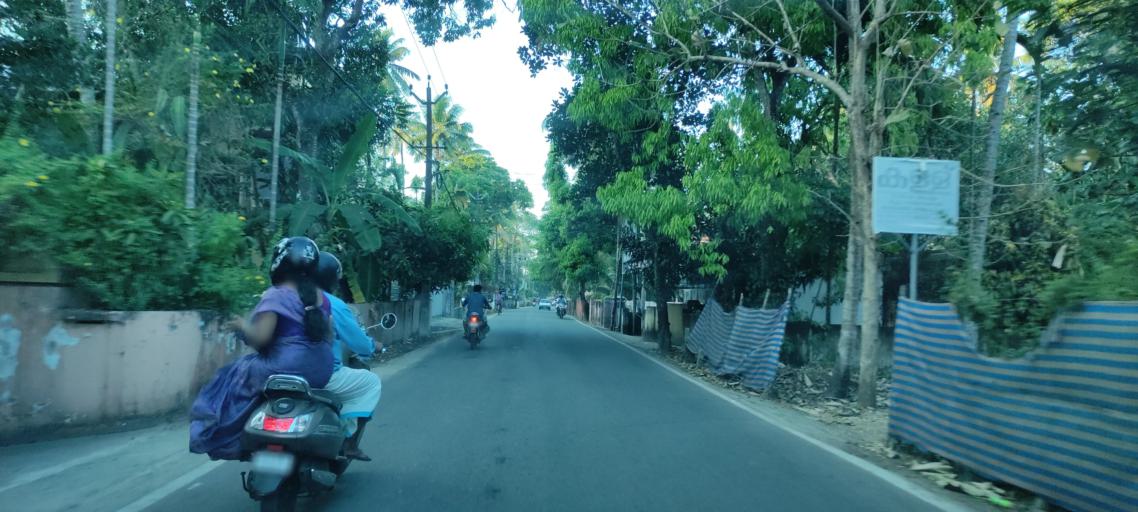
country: IN
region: Kerala
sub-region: Alappuzha
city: Kayankulam
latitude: 9.2207
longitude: 76.4605
